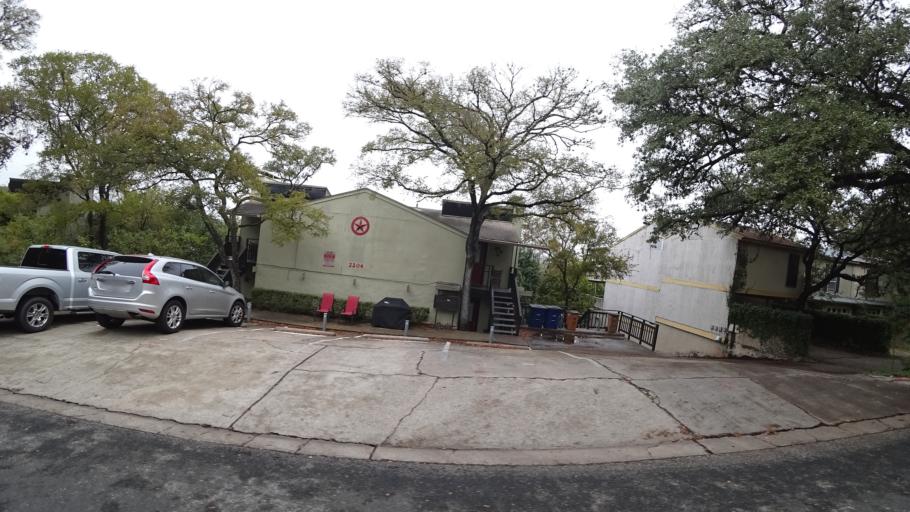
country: US
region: Texas
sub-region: Travis County
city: Rollingwood
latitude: 30.2596
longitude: -97.7730
